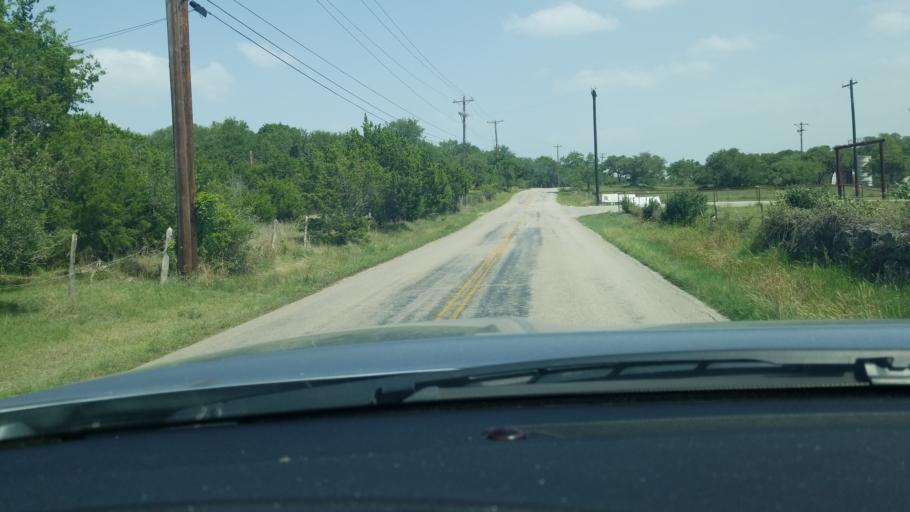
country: US
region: Texas
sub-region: Comal County
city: Bulverde
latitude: 29.7778
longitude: -98.4606
